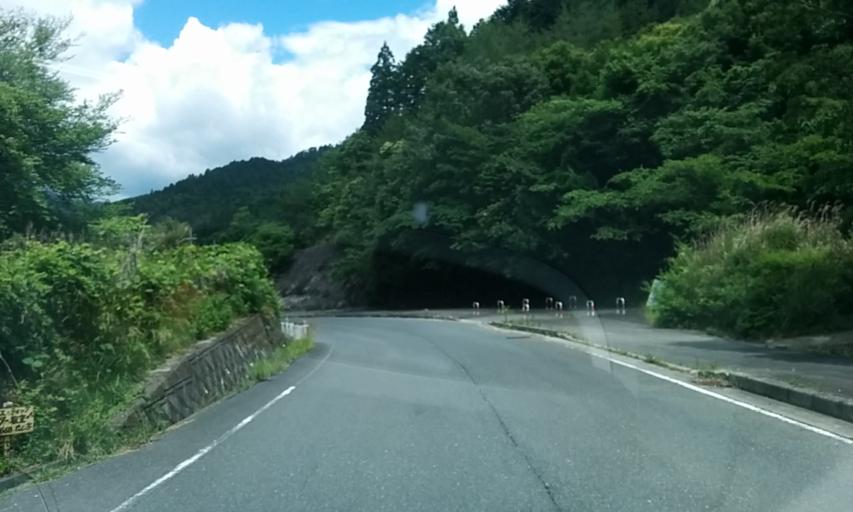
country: JP
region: Kyoto
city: Kameoka
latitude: 35.0108
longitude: 135.4521
